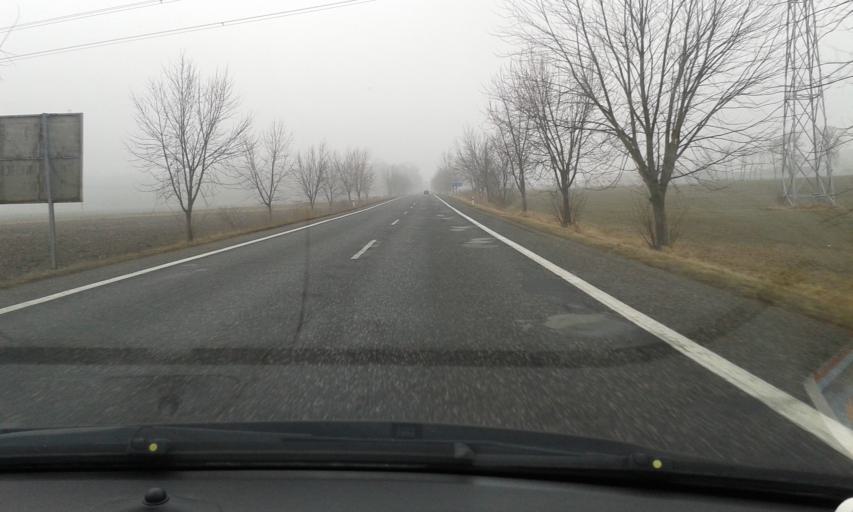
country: SK
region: Banskobystricky
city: Dudince
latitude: 48.1356
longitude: 18.8753
